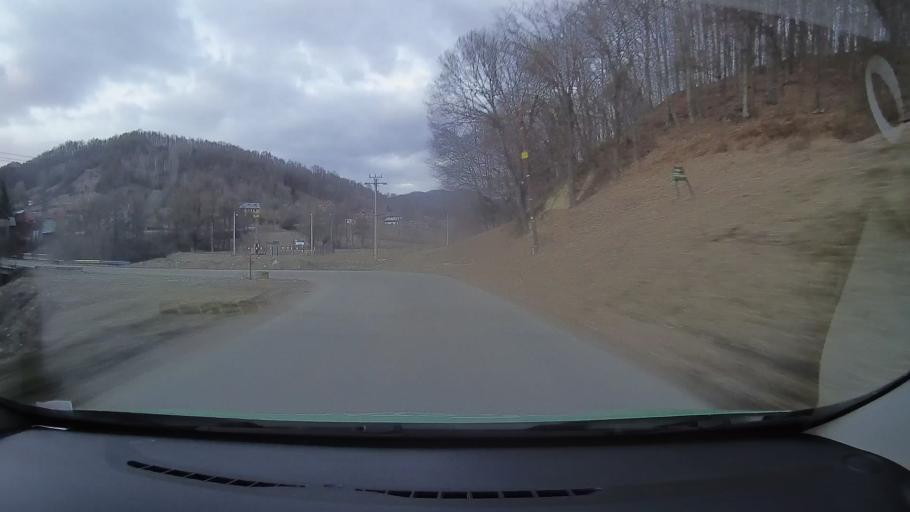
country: RO
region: Dambovita
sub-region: Comuna Visinesti
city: Visinesti
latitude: 45.0975
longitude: 25.5792
